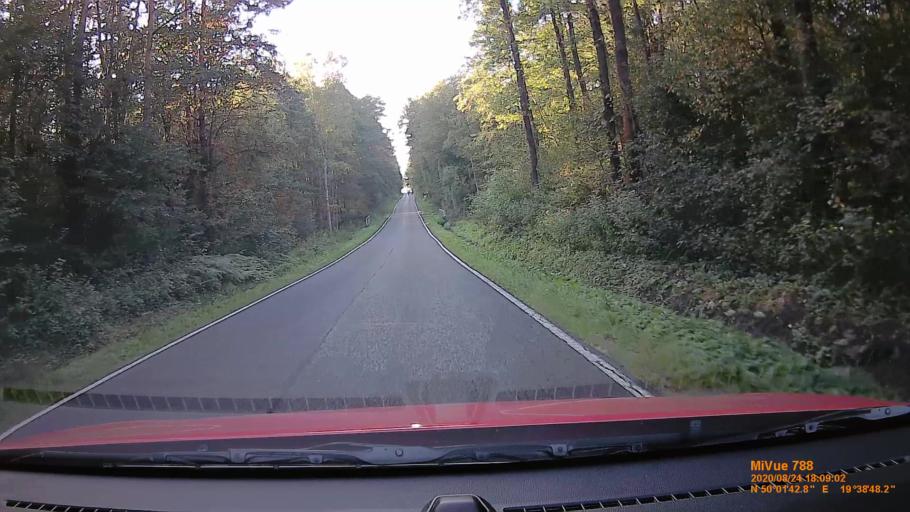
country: PL
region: Lesser Poland Voivodeship
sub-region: Powiat krakowski
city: Sanka
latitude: 50.0286
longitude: 19.6467
